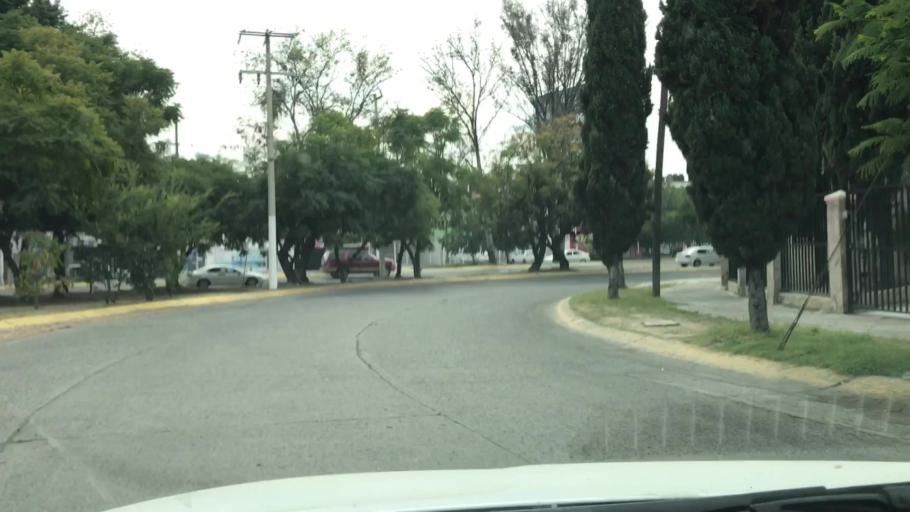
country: MX
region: Jalisco
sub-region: Tlajomulco de Zuniga
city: Palomar
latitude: 20.6316
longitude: -103.4325
